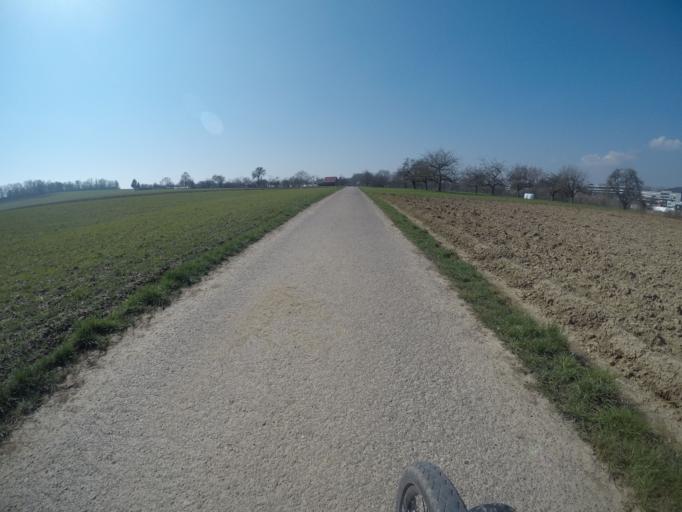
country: DE
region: Baden-Wuerttemberg
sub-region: Tuebingen Region
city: Sickenhausen
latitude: 48.5423
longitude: 9.1777
